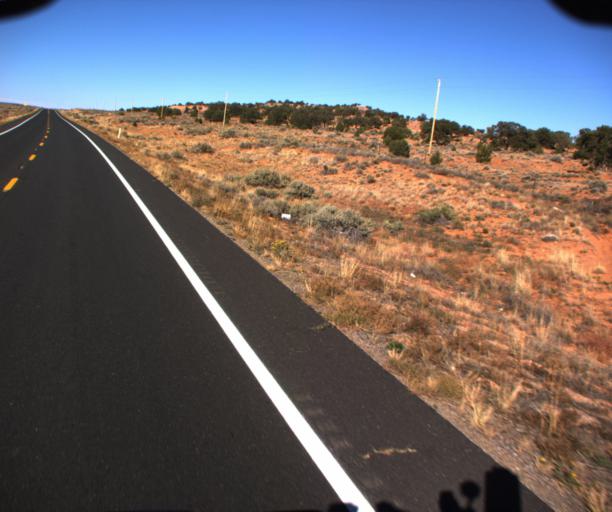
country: US
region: Arizona
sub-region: Coconino County
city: Kaibito
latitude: 36.5283
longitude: -110.7014
